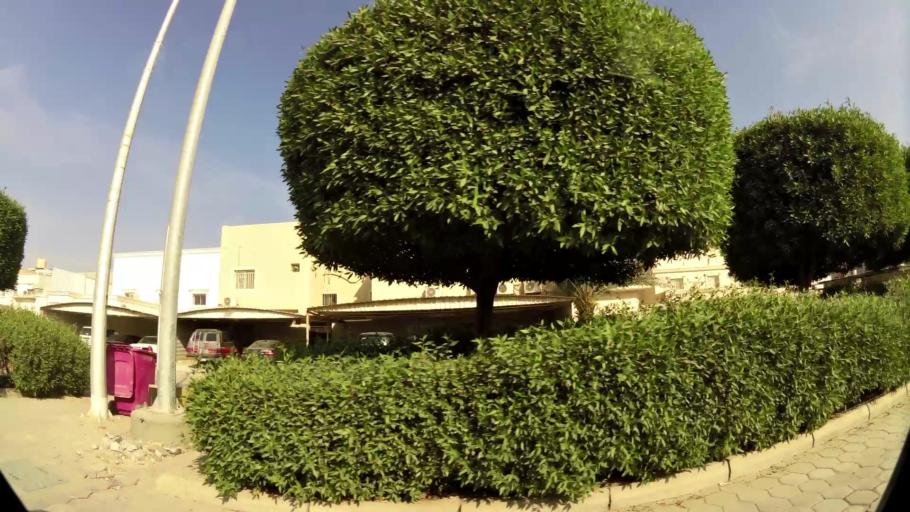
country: KW
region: Al Ahmadi
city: Ar Riqqah
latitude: 29.1483
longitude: 48.1059
